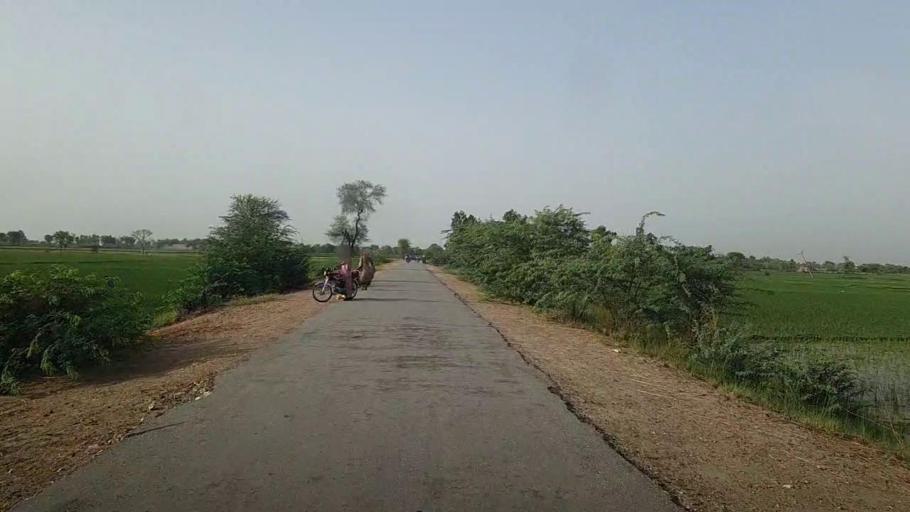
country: PK
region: Sindh
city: Khairpur Nathan Shah
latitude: 27.1233
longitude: 67.7895
